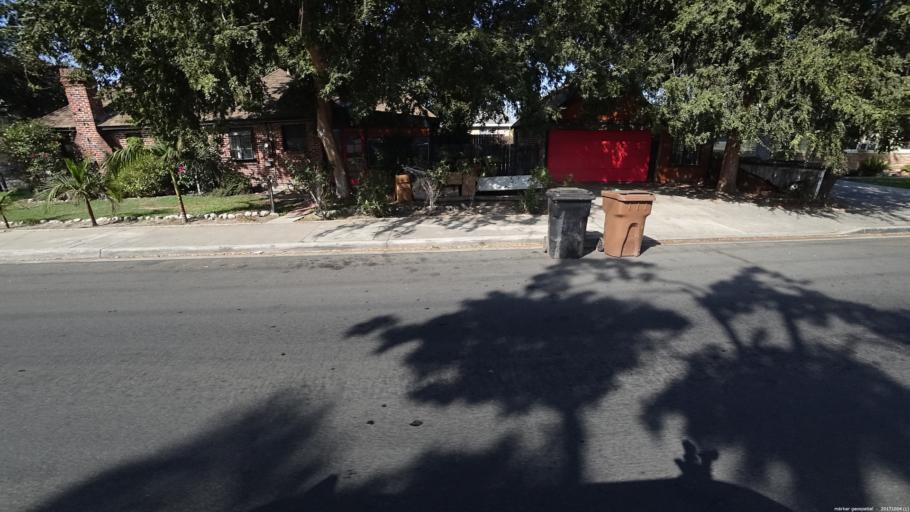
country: US
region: California
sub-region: Orange County
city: Garden Grove
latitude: 33.7781
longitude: -117.9323
